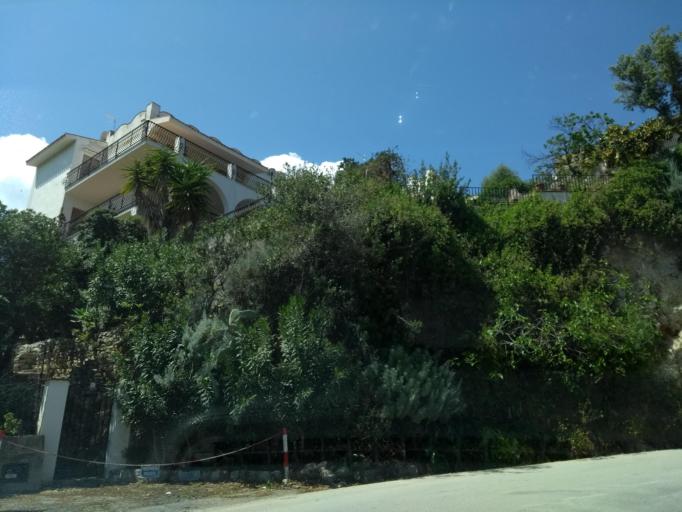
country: IT
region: Sicily
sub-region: Trapani
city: Castellammare del Golfo
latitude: 38.0563
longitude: 12.8359
